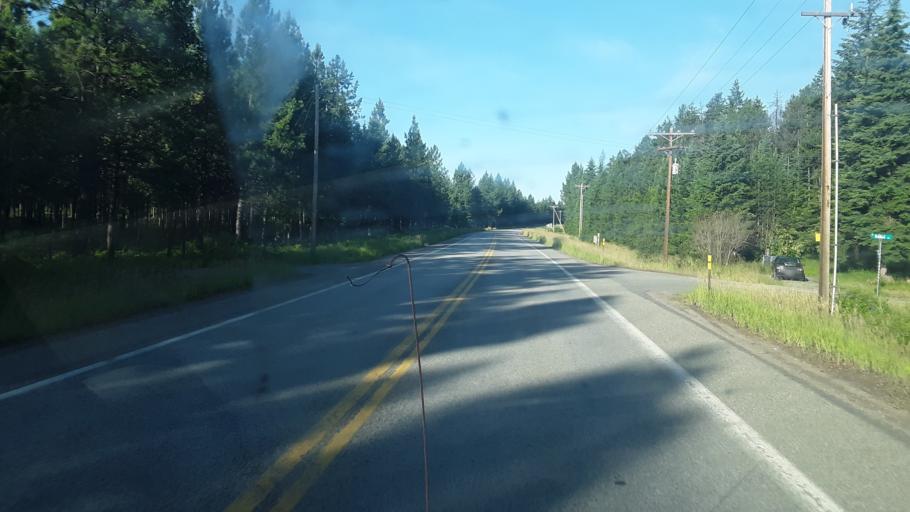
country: US
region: Idaho
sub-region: Boundary County
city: Bonners Ferry
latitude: 48.7314
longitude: -116.1919
